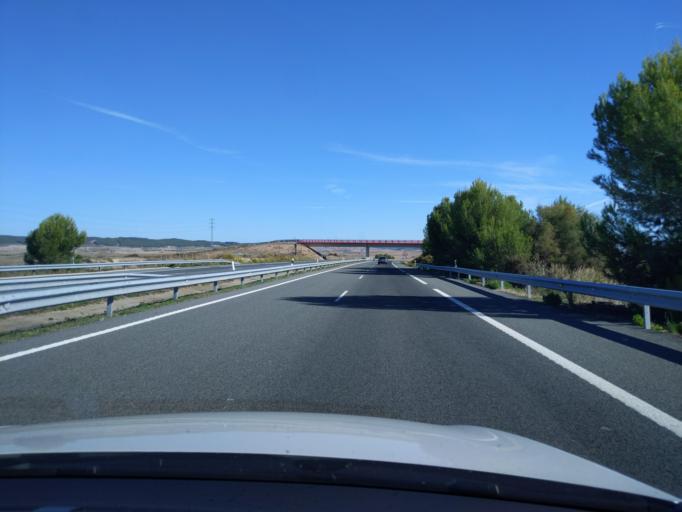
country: ES
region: Navarre
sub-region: Provincia de Navarra
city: Los Arcos
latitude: 42.5345
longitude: -2.2178
